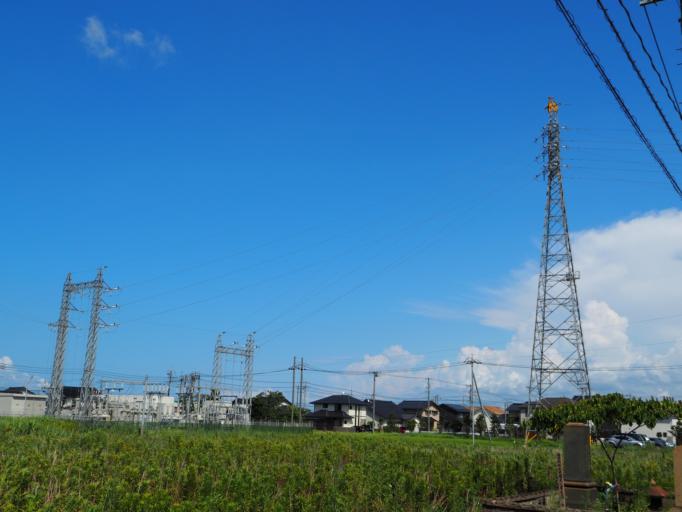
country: JP
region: Shimane
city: Hiratacho
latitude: 35.4332
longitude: 132.8258
